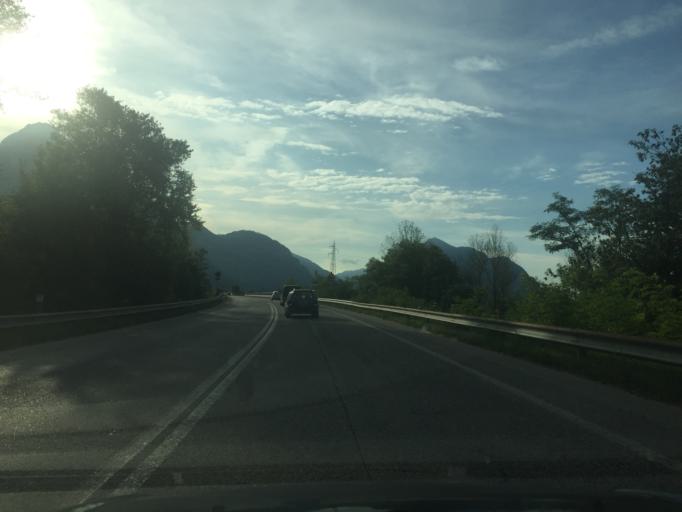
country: IT
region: Friuli Venezia Giulia
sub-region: Provincia di Udine
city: Chiaulis
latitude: 46.4024
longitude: 12.9980
